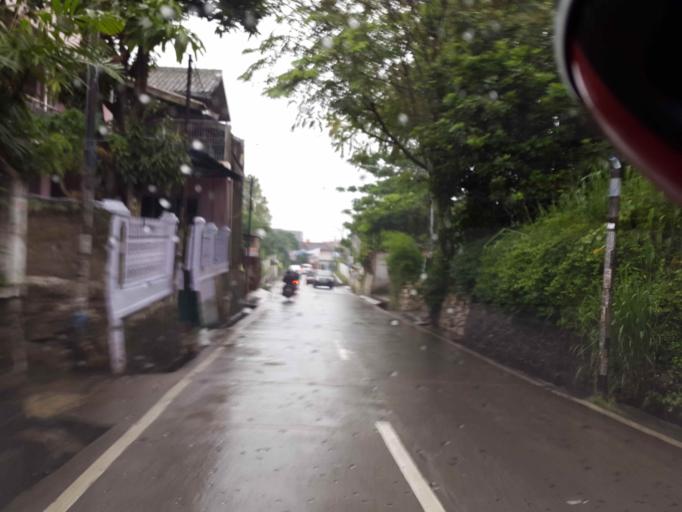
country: ID
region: West Java
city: Cimahi
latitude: -6.8843
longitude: 107.5573
